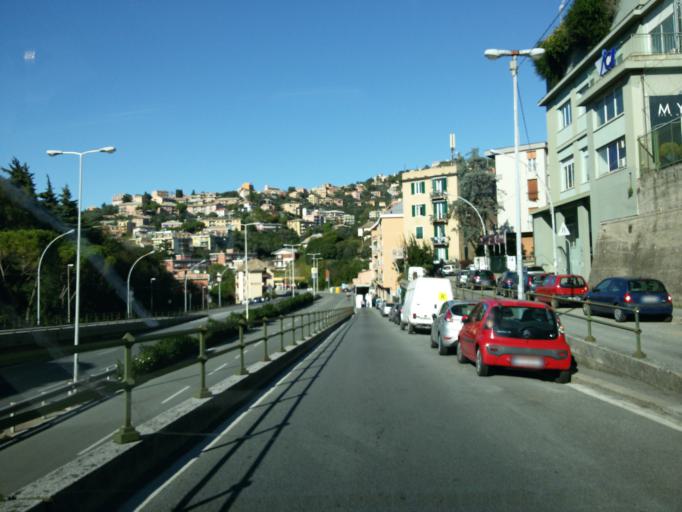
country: IT
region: Liguria
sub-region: Provincia di Genova
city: Bogliasco
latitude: 44.3963
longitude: 8.9936
